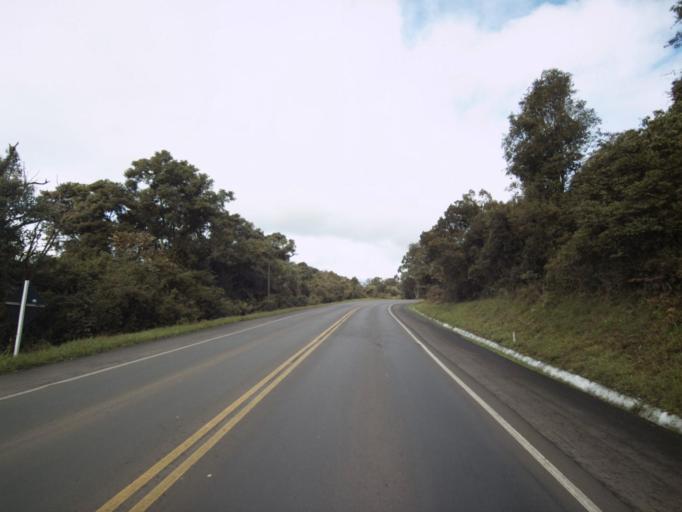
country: BR
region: Santa Catarina
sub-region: Concordia
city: Concordia
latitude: -27.1994
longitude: -51.9397
